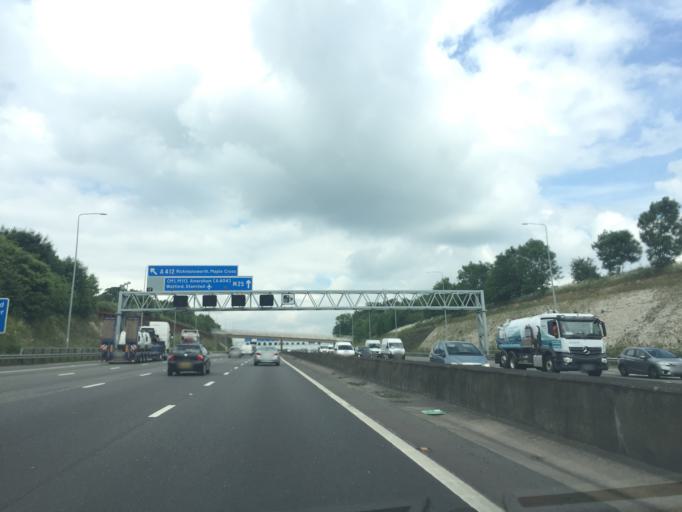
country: GB
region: England
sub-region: Hertfordshire
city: Chorleywood
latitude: 51.6315
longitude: -0.5174
